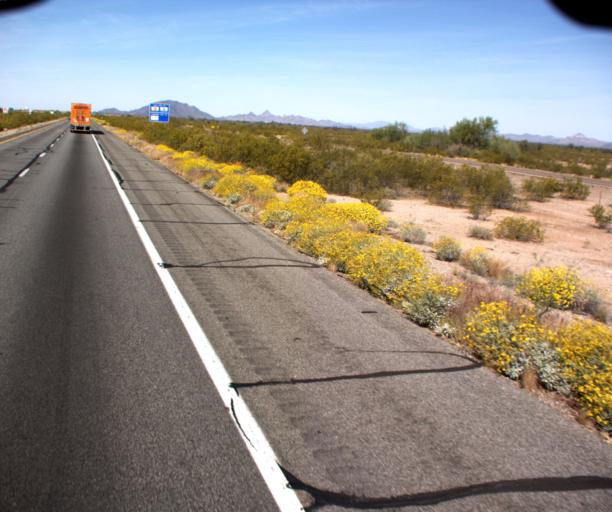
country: US
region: Arizona
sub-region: Maricopa County
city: Buckeye
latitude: 33.4937
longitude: -112.9197
